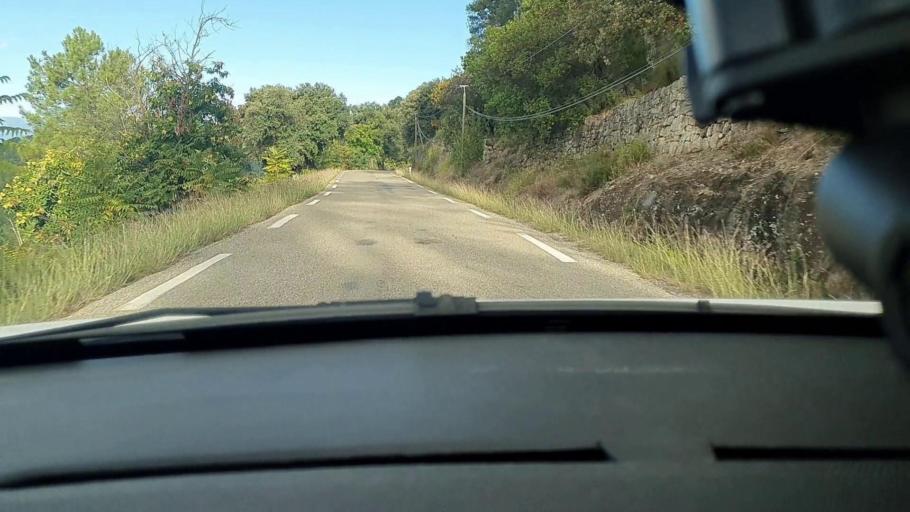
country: FR
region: Languedoc-Roussillon
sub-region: Departement du Gard
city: Besseges
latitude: 44.3081
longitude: 4.0806
